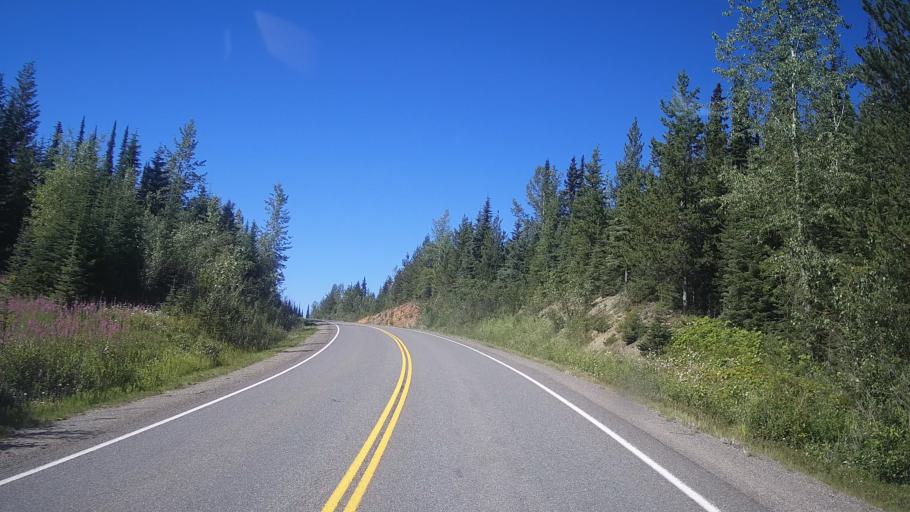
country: CA
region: British Columbia
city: Kamloops
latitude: 51.5029
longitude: -120.3564
